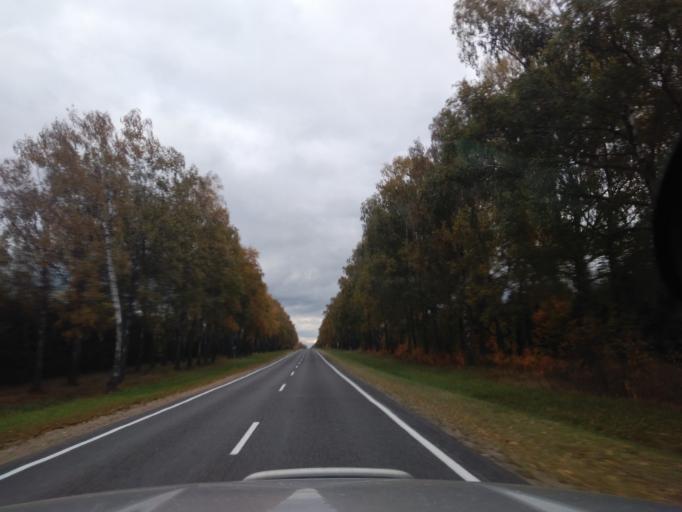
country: BY
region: Minsk
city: Slutsk
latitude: 53.2215
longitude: 27.5007
